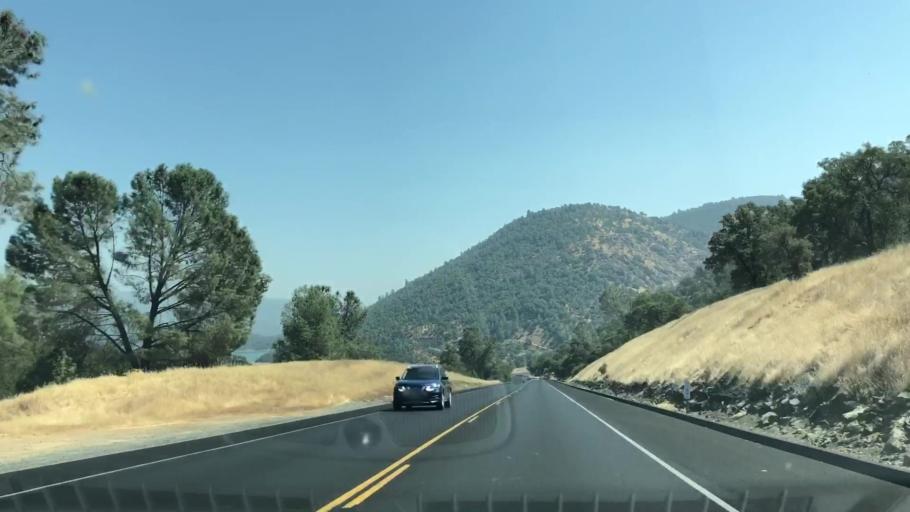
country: US
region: California
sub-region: Tuolumne County
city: Jamestown
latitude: 37.8477
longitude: -120.3874
